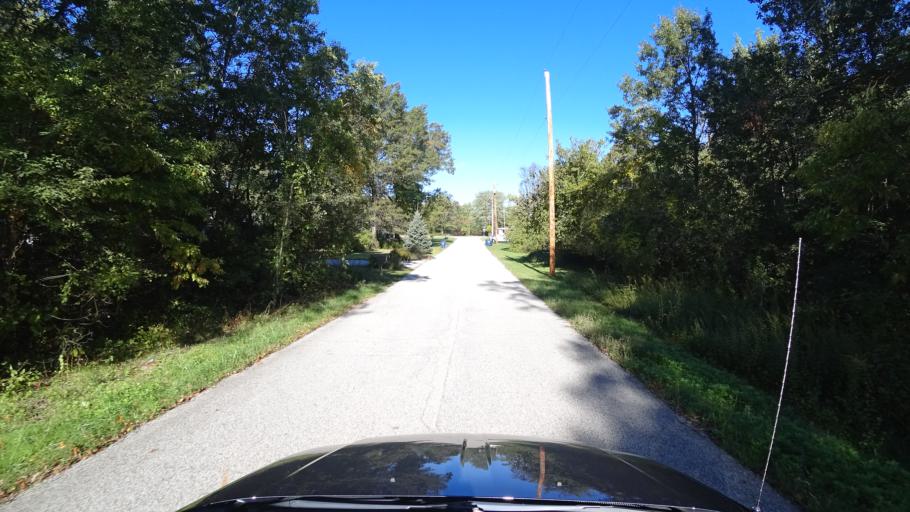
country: US
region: Indiana
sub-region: LaPorte County
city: Michigan City
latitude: 41.6965
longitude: -86.9279
